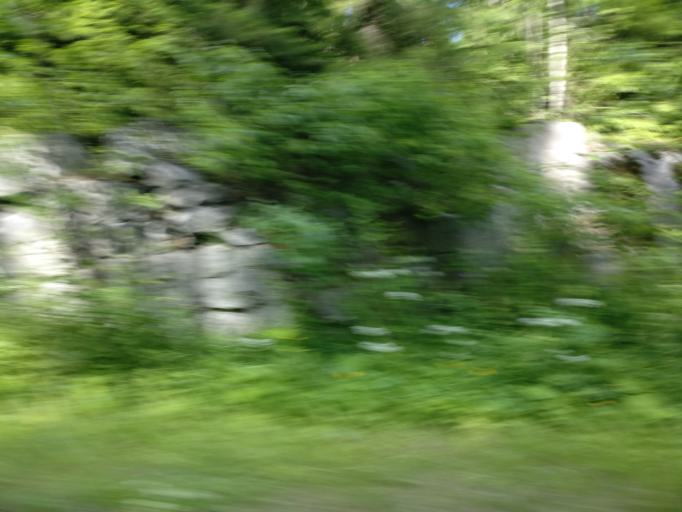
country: FI
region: Southern Savonia
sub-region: Savonlinna
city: Kerimaeki
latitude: 61.8253
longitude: 29.2431
